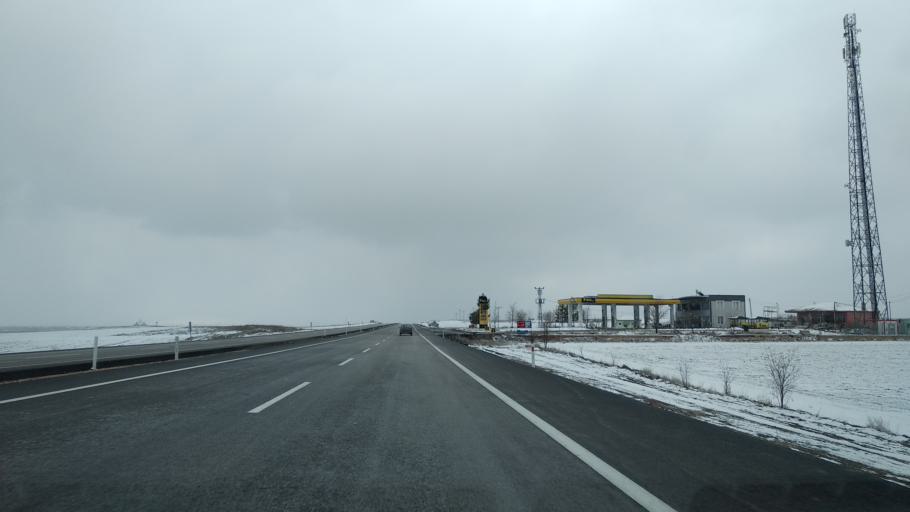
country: TR
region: Kayseri
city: Elbasi
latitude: 38.6520
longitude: 35.9985
